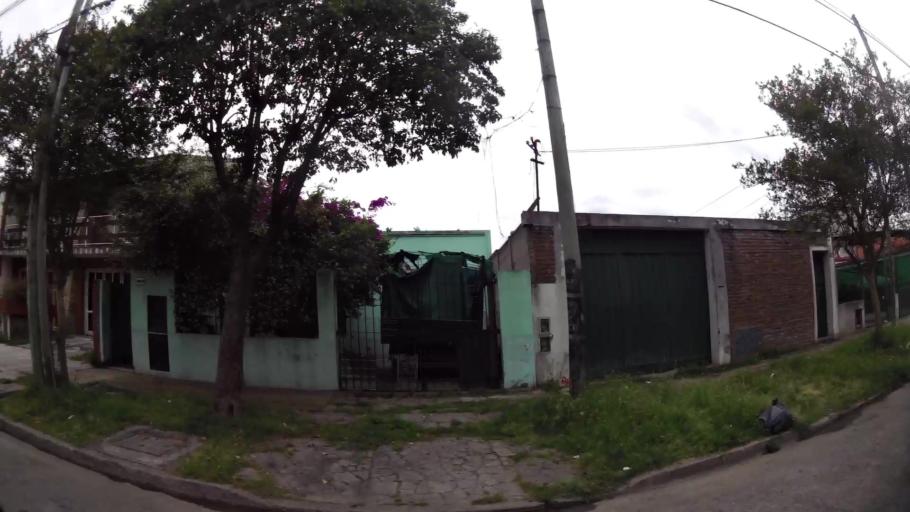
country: AR
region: Buenos Aires
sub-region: Partido de Lanus
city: Lanus
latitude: -34.6901
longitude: -58.3718
